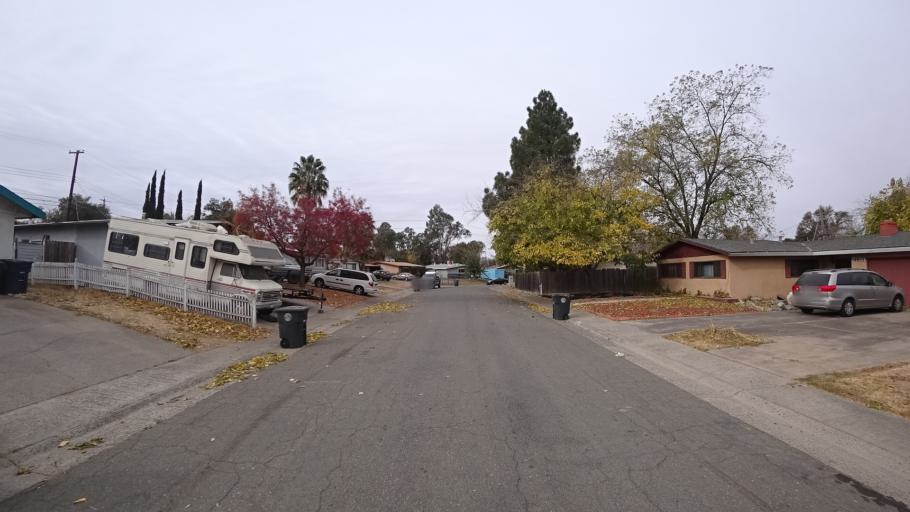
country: US
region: California
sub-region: Sacramento County
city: Antelope
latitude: 38.7079
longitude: -121.3065
